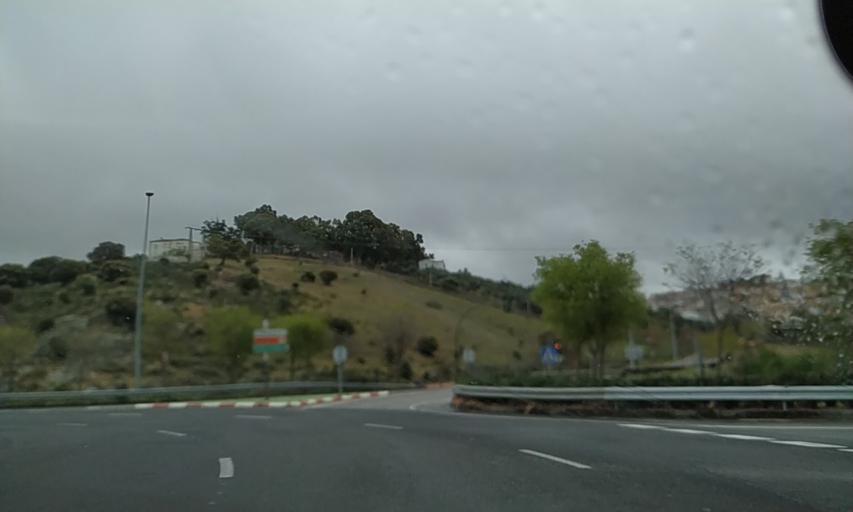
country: ES
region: Extremadura
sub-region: Provincia de Caceres
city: Caceres
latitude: 39.4858
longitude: -6.3826
